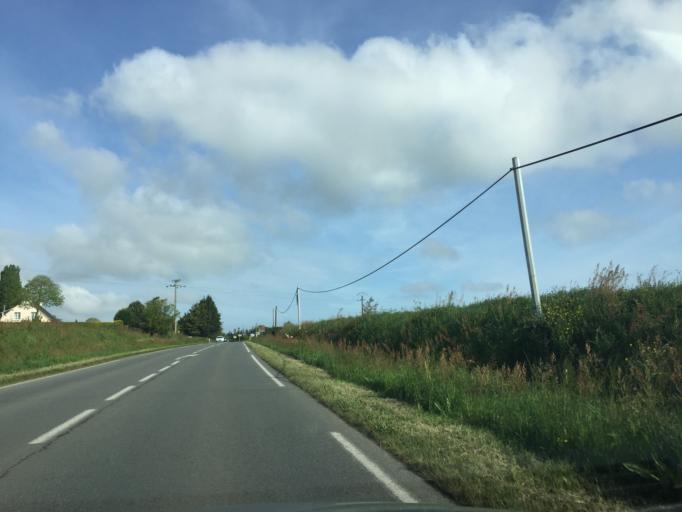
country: FR
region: Brittany
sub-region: Departement des Cotes-d'Armor
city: Saint-Cast-le-Guildo
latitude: 48.5900
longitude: -2.2454
